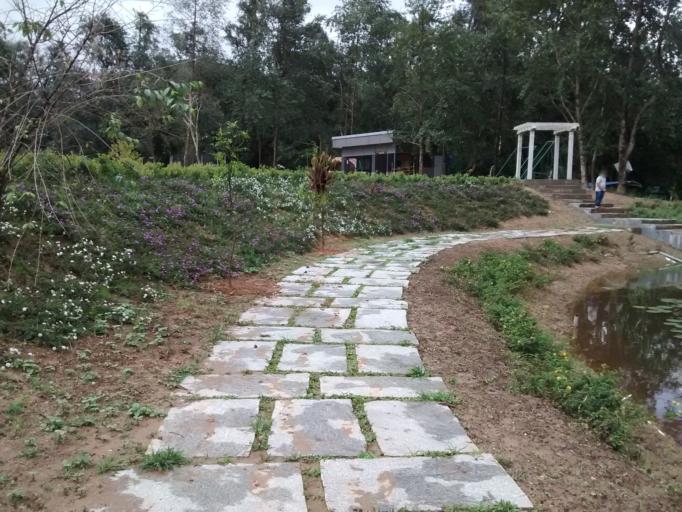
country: IN
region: Kerala
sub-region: Idukki
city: Munnar
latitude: 10.0700
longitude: 77.0661
